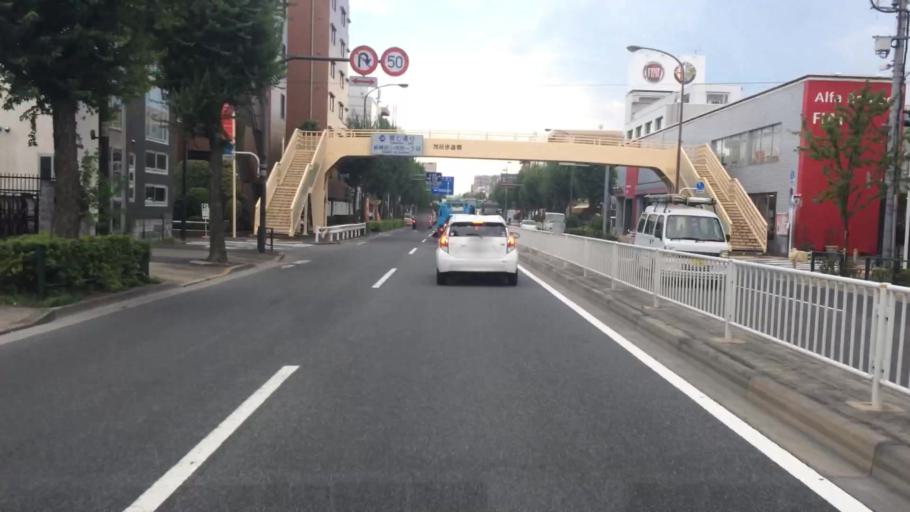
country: JP
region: Tokyo
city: Tokyo
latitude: 35.7469
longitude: 139.6767
